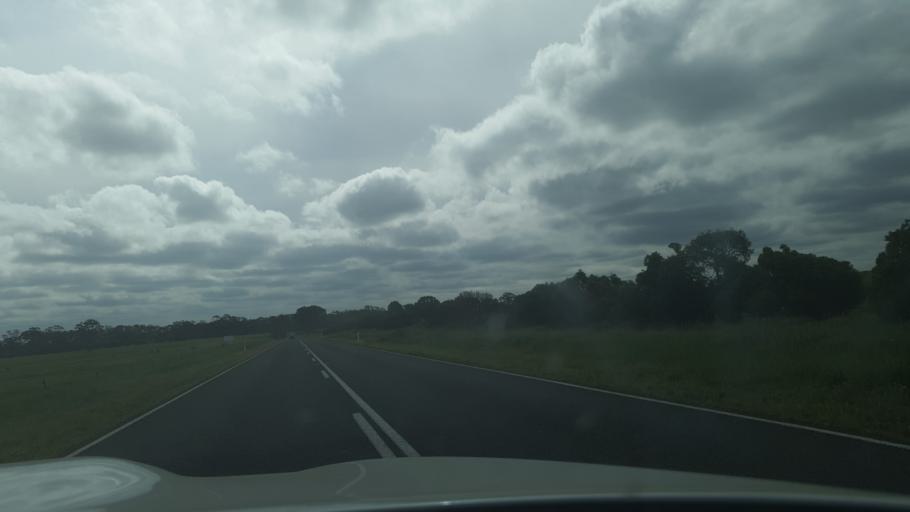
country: AU
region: Victoria
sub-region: Central Goldfields
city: Maryborough
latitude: -37.2074
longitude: 143.7169
